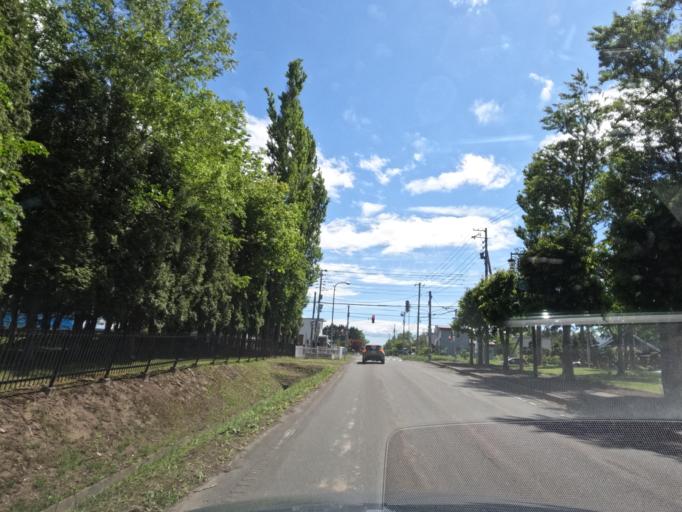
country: JP
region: Hokkaido
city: Kitahiroshima
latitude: 42.9994
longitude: 141.7238
